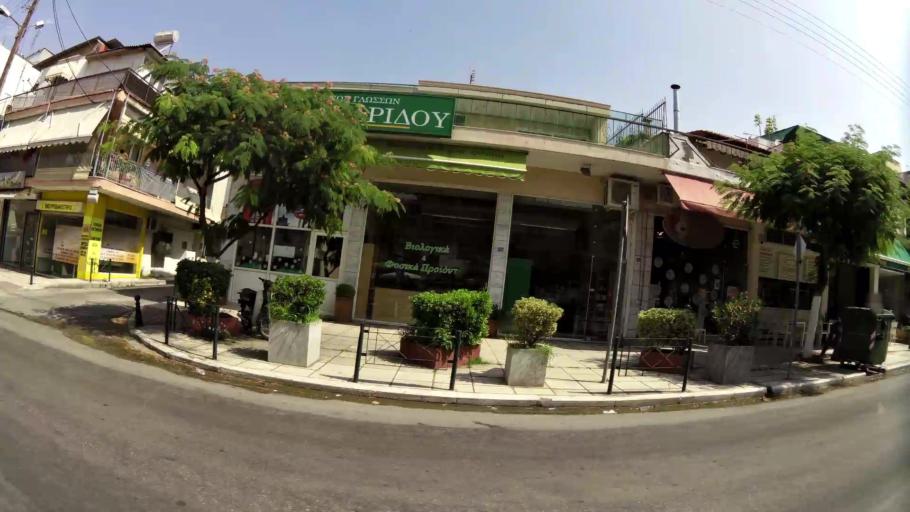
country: GR
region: Central Macedonia
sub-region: Nomos Thessalonikis
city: Evosmos
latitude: 40.6666
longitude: 22.9212
